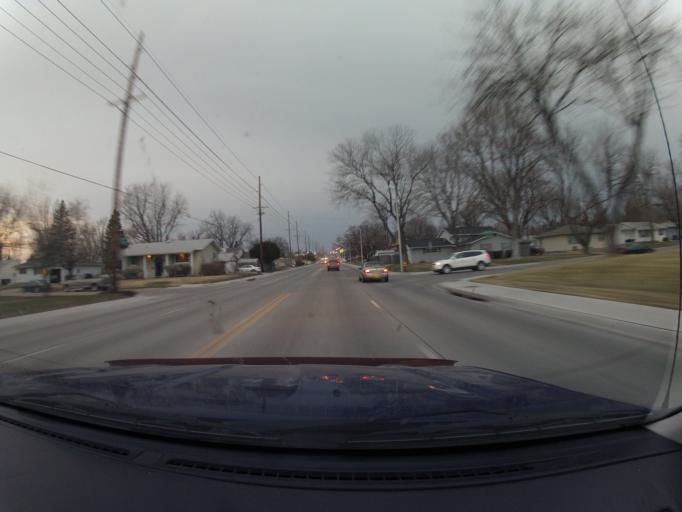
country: US
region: Nebraska
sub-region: Buffalo County
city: Kearney
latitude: 40.7139
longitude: -99.0749
